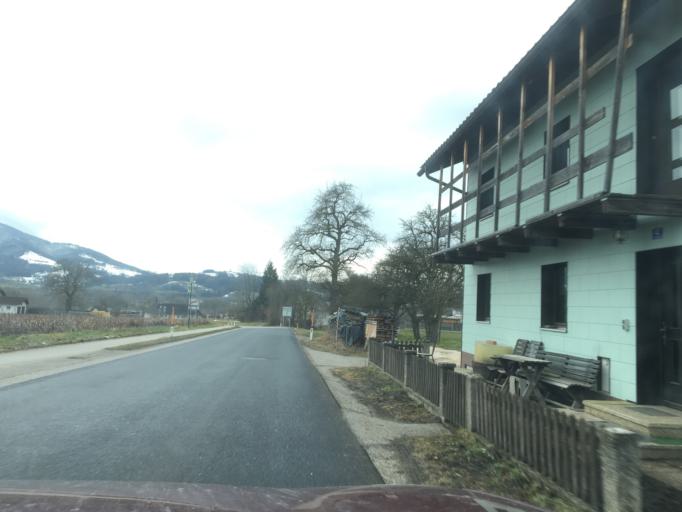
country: AT
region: Upper Austria
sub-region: Politischer Bezirk Kirchdorf an der Krems
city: Micheldorf in Oberoesterreich
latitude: 47.9432
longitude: 14.1224
